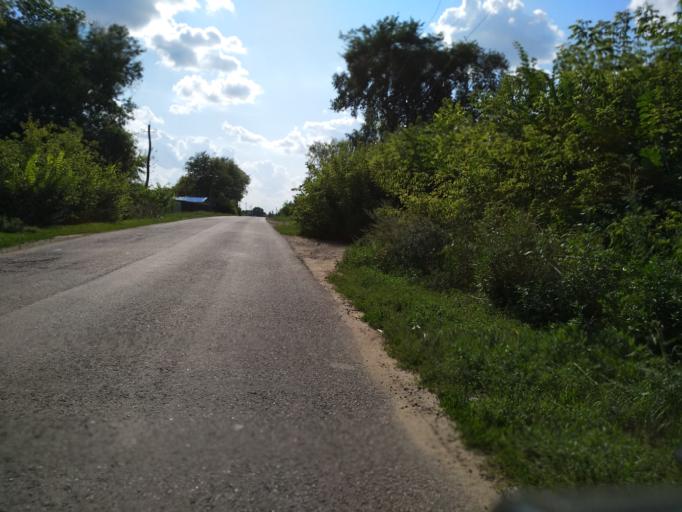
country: RU
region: Lipetsk
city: Dobrinka
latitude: 52.0396
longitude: 40.5476
